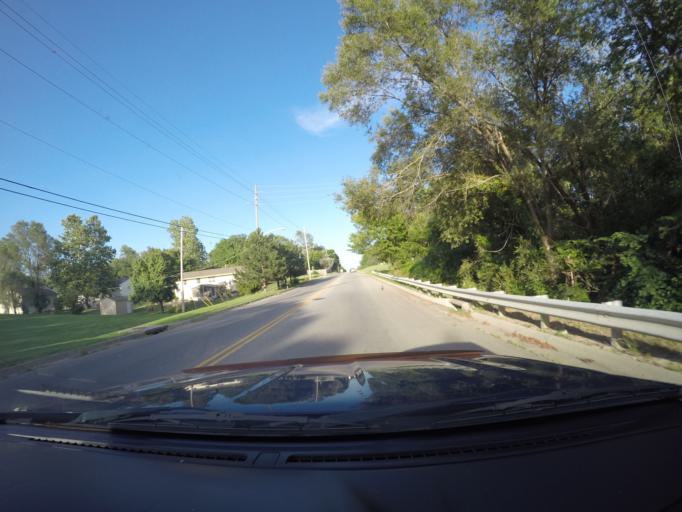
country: US
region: Kansas
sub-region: Wyandotte County
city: Edwardsville
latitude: 39.1432
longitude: -94.7784
